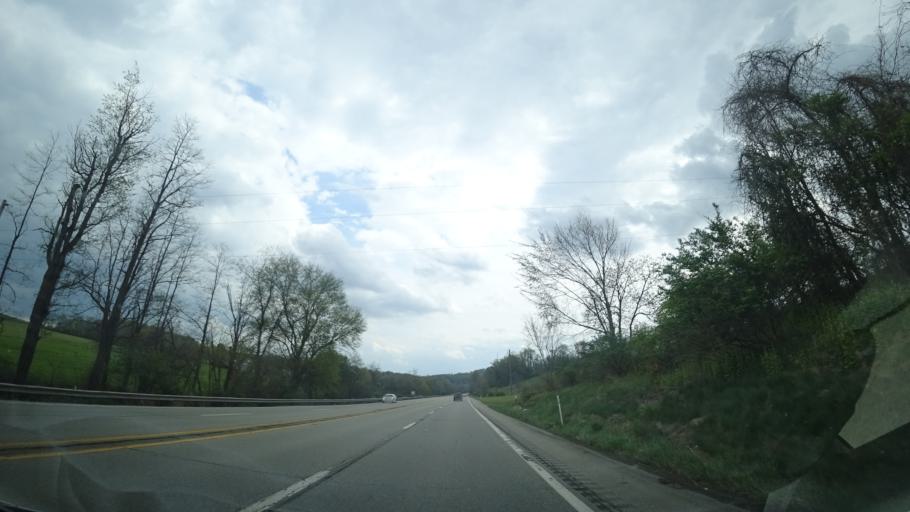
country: US
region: Pennsylvania
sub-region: Fayette County
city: Perryopolis
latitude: 40.0383
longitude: -79.7699
